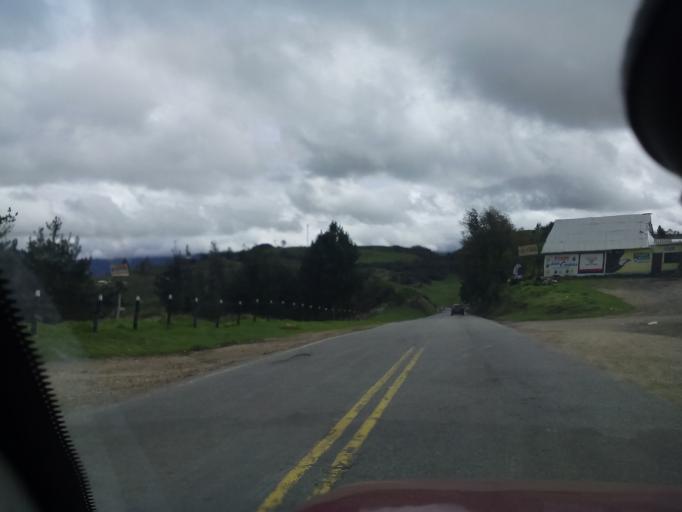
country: CO
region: Boyaca
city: Combita
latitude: 5.6531
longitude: -73.3531
